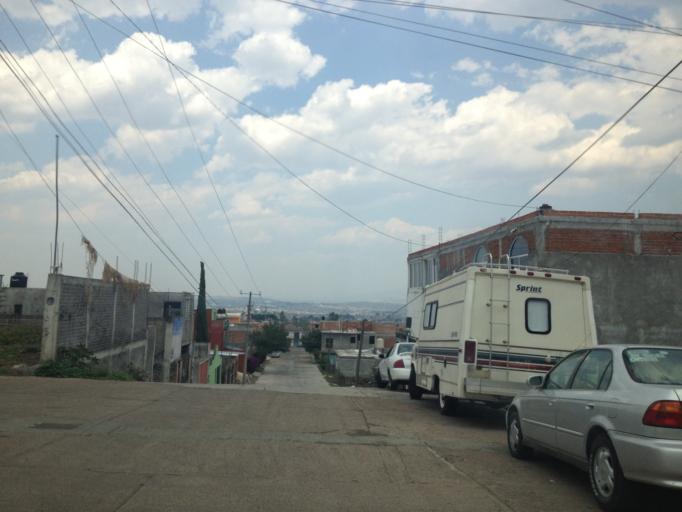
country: MX
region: Michoacan
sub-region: Morelia
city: San Antonio
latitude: 19.7087
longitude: -101.2463
